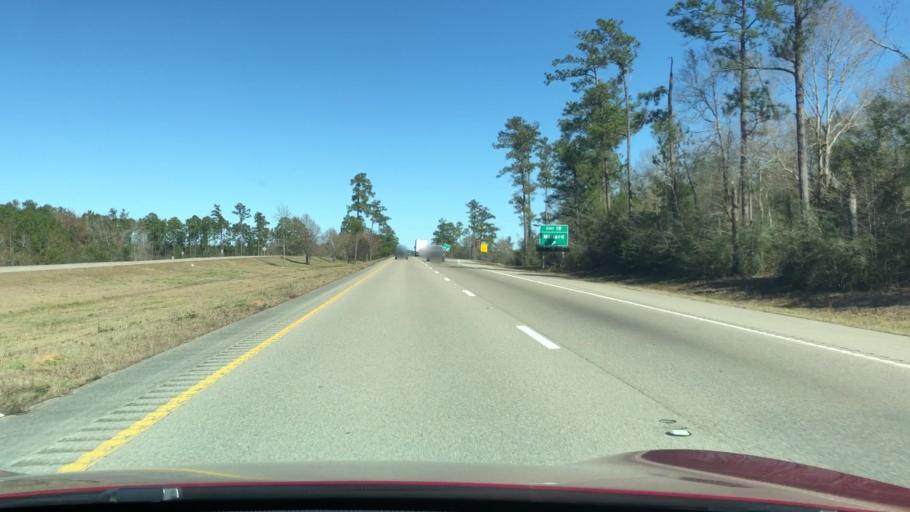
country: US
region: Mississippi
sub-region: Pearl River County
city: Poplarville
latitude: 30.7141
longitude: -89.5561
